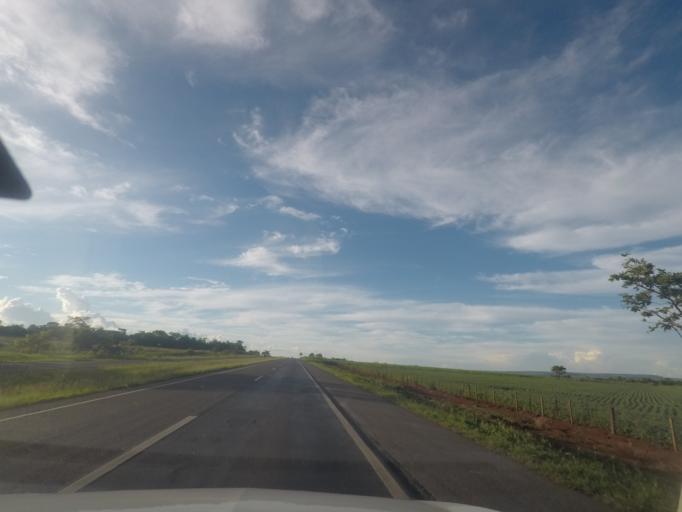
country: BR
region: Goias
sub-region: Goiatuba
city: Goiatuba
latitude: -18.1982
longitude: -49.2815
